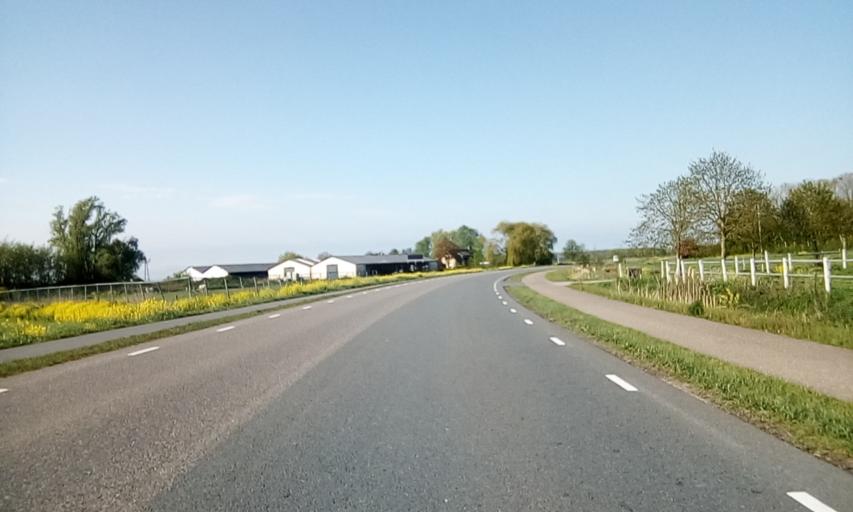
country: NL
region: Gelderland
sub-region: Gemeente Druten
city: Druten
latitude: 51.8775
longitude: 5.5637
